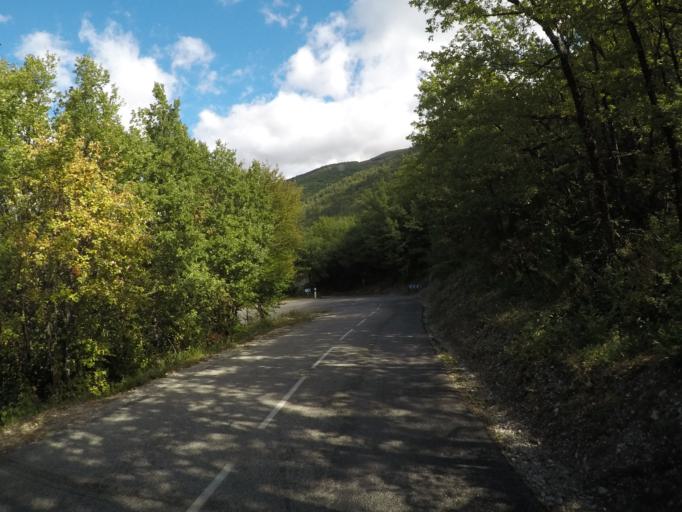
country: FR
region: Provence-Alpes-Cote d'Azur
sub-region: Departement du Vaucluse
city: Sault
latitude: 44.1641
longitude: 5.4481
